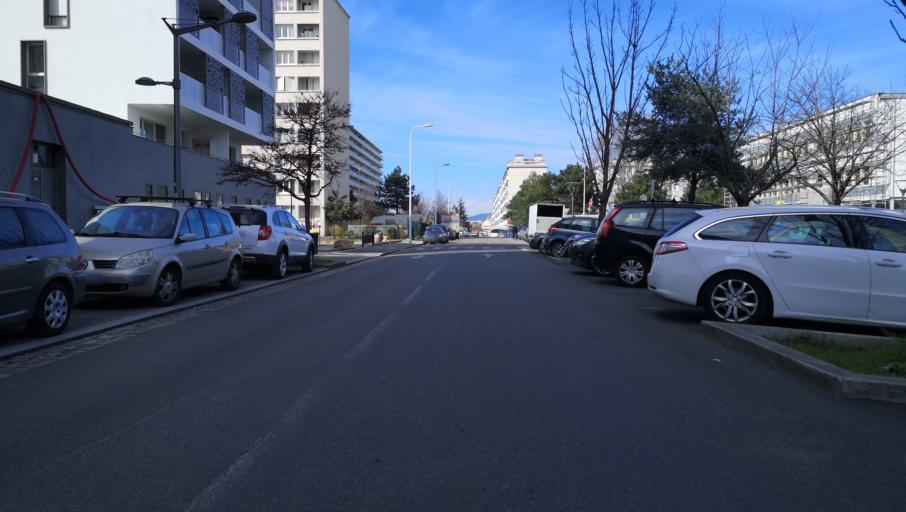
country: FR
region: Rhone-Alpes
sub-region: Departement du Rhone
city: Saint-Fons
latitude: 45.7295
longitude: 4.8651
